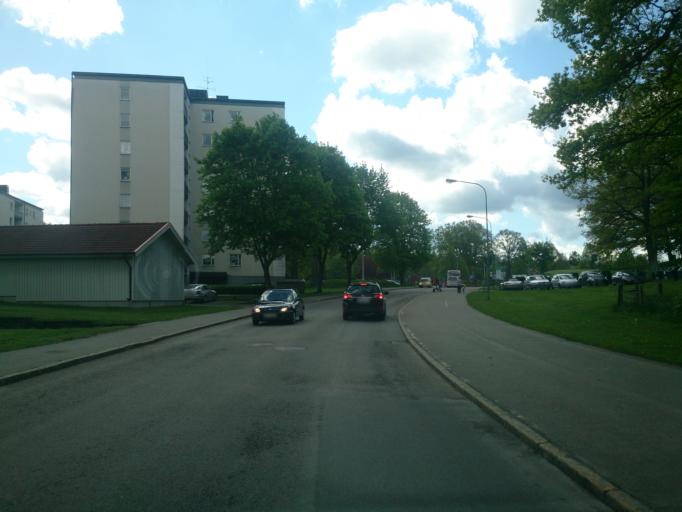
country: SE
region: OEstergoetland
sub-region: Atvidabergs Kommun
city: Atvidaberg
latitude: 58.1928
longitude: 16.0027
